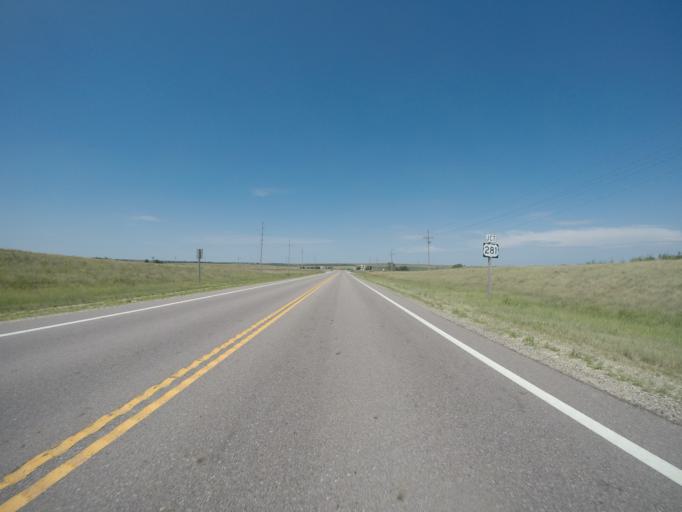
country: US
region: Kansas
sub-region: Osborne County
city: Osborne
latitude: 39.5100
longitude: -98.6887
